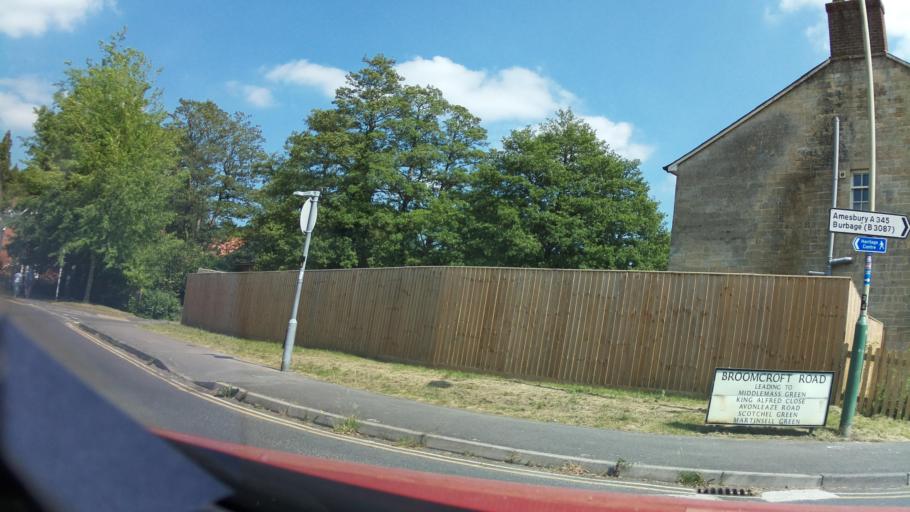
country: GB
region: England
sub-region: Wiltshire
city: Pewsey
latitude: 51.3409
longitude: -1.7668
